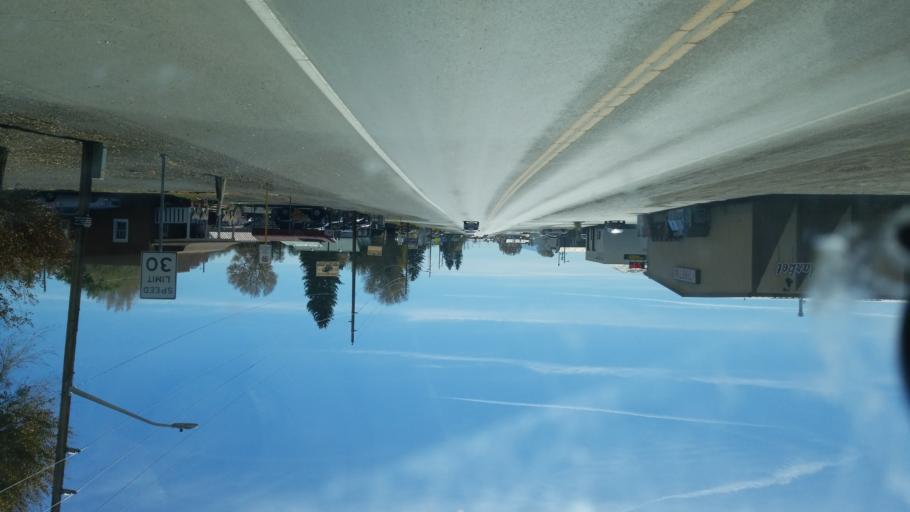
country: US
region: Colorado
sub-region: Conejos County
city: Conejos
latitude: 37.2782
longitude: -105.9611
